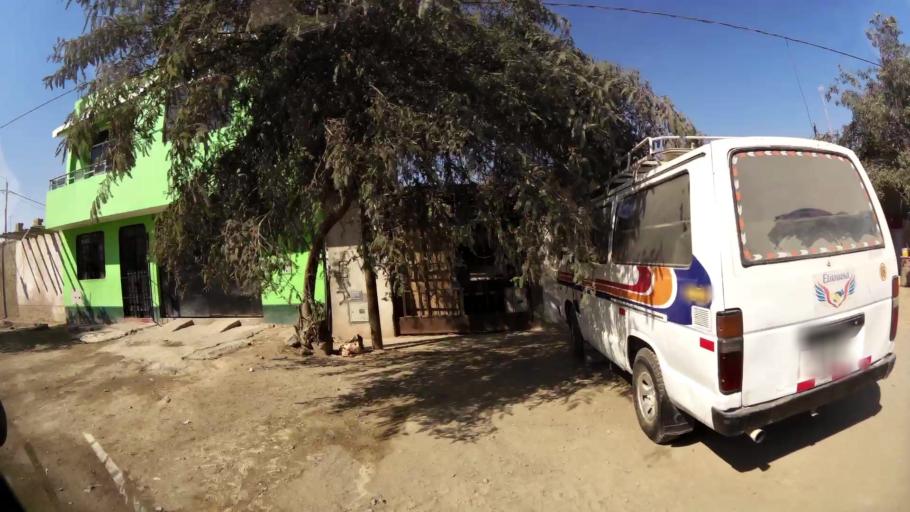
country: PE
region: Ica
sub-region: Provincia de Ica
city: La Tinguina
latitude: -14.0372
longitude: -75.7022
